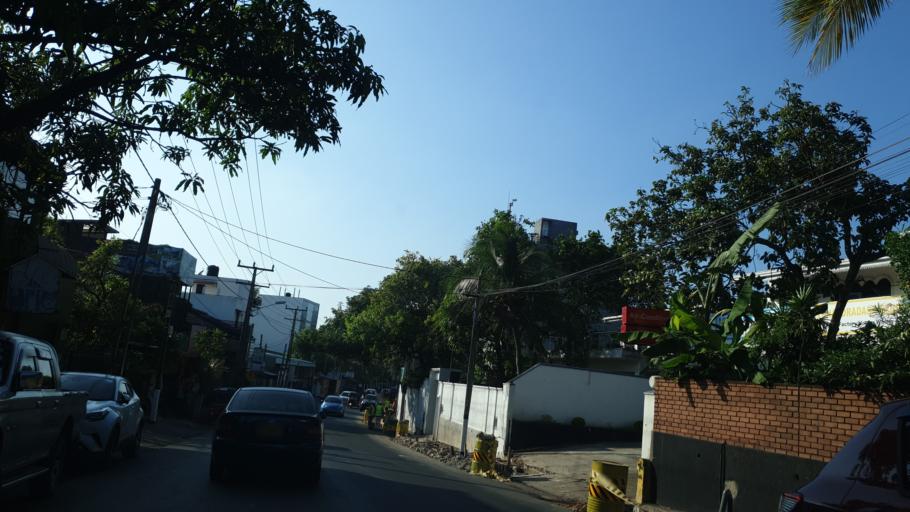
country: LK
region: Western
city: Sri Jayewardenepura Kotte
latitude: 6.8732
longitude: 79.9039
